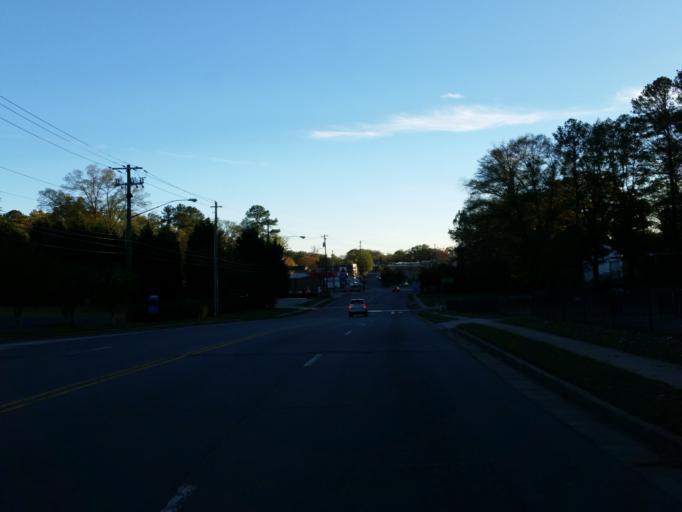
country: US
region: Georgia
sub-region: Cobb County
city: Marietta
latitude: 33.9552
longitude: -84.5346
